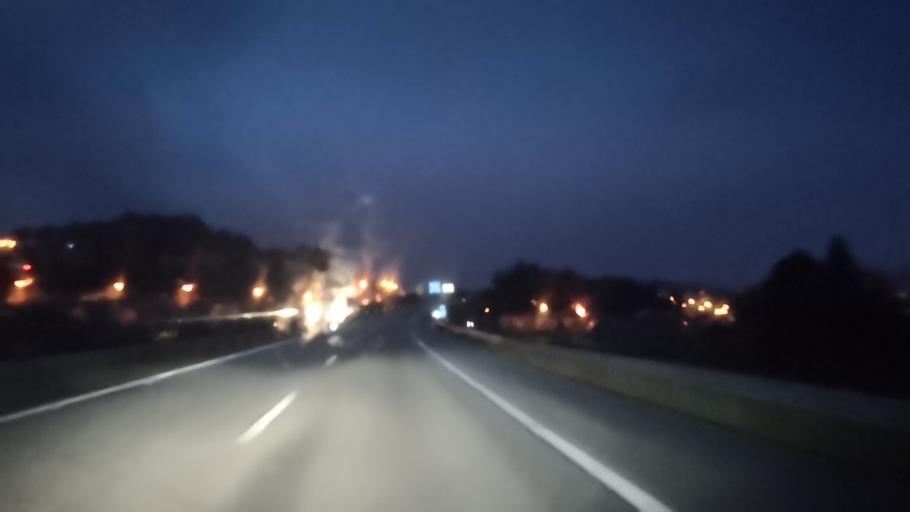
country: PT
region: Braga
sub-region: Guimaraes
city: Urgeses
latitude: 41.4108
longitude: -8.2927
